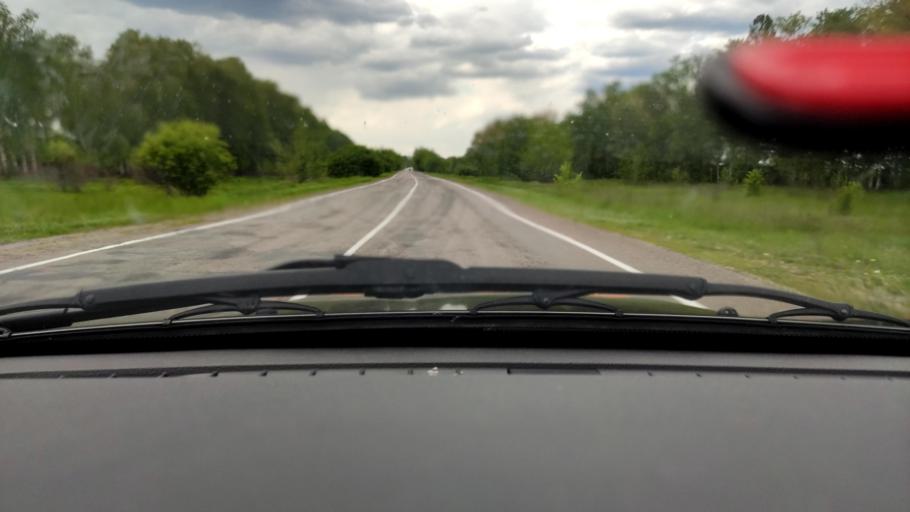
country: RU
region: Belgorod
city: Krasnoye
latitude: 51.0564
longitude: 38.8966
